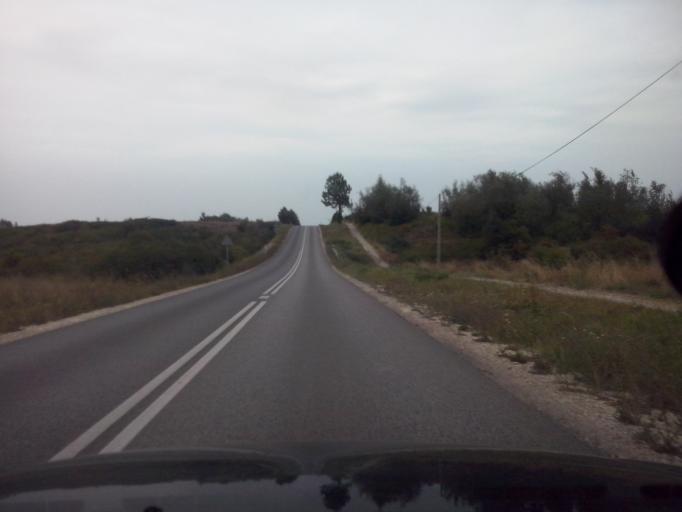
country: PL
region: Swietokrzyskie
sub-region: Powiat kielecki
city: Morawica
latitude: 50.6916
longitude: 20.5975
